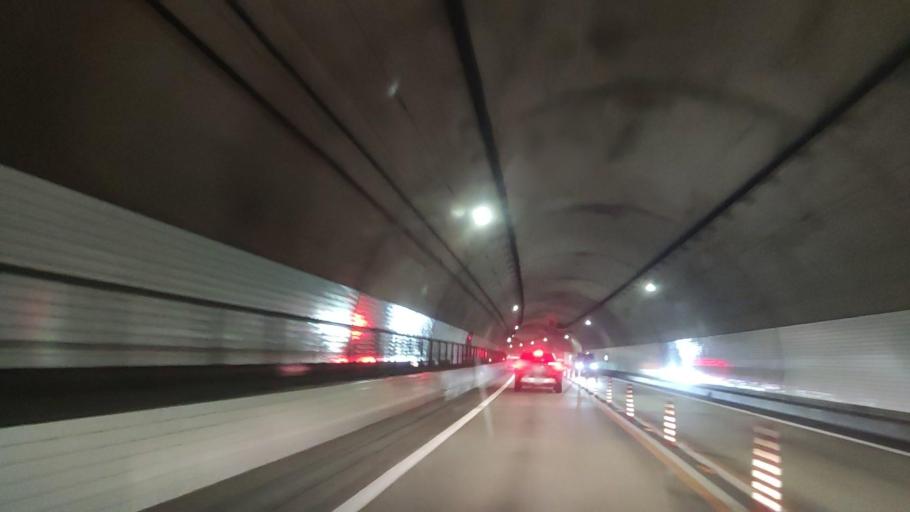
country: JP
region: Kyoto
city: Miyazu
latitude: 35.5569
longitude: 135.1258
